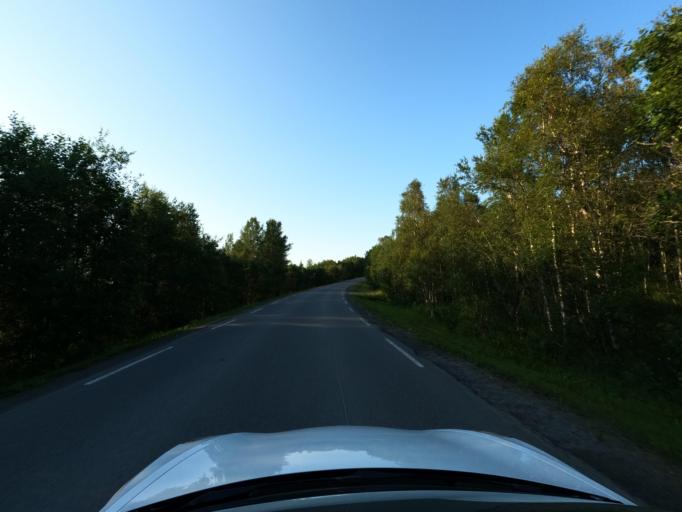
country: NO
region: Troms
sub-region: Skanland
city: Evenskjer
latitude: 68.4857
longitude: 16.7119
